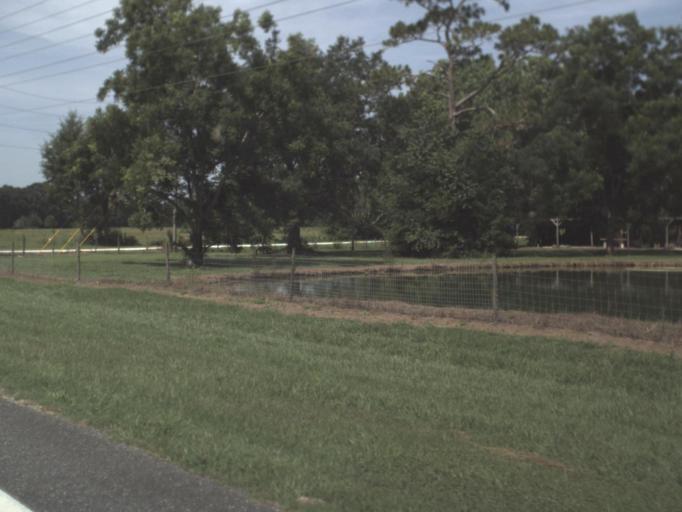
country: US
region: Florida
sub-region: Lafayette County
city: Mayo
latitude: 30.1447
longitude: -83.1653
